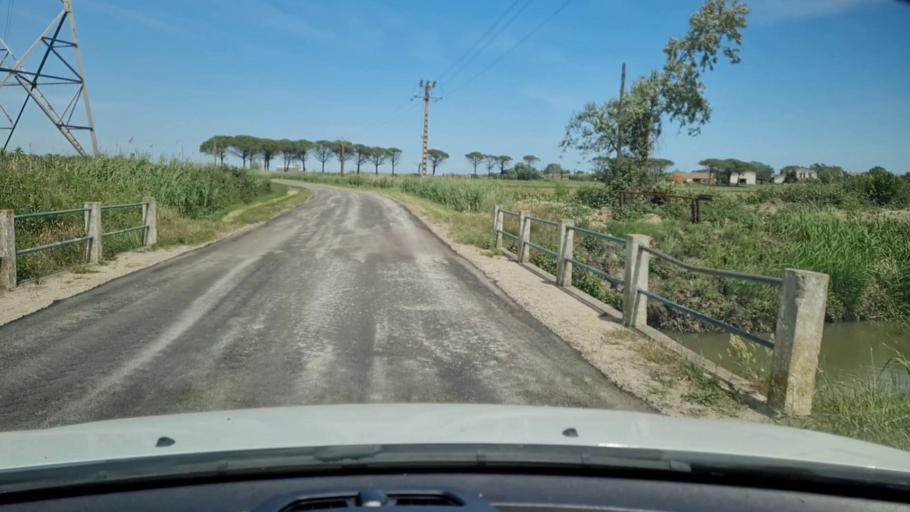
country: FR
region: Languedoc-Roussillon
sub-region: Departement du Gard
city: Saint-Gilles
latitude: 43.5719
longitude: 4.3960
